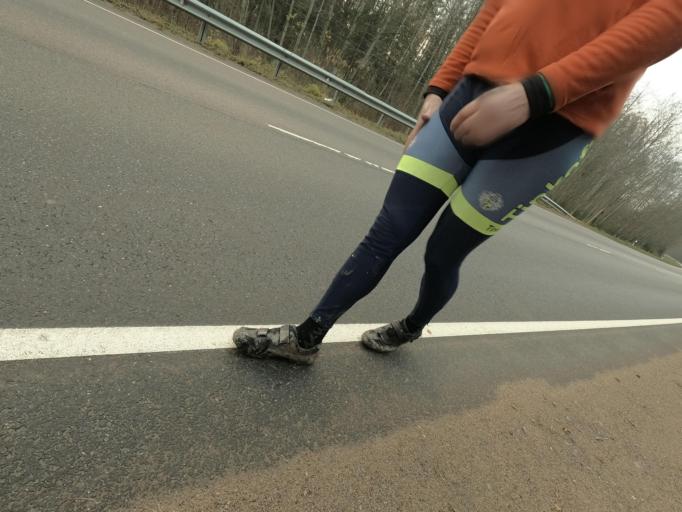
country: RU
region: Leningrad
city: Pavlovo
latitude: 59.8088
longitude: 30.9617
